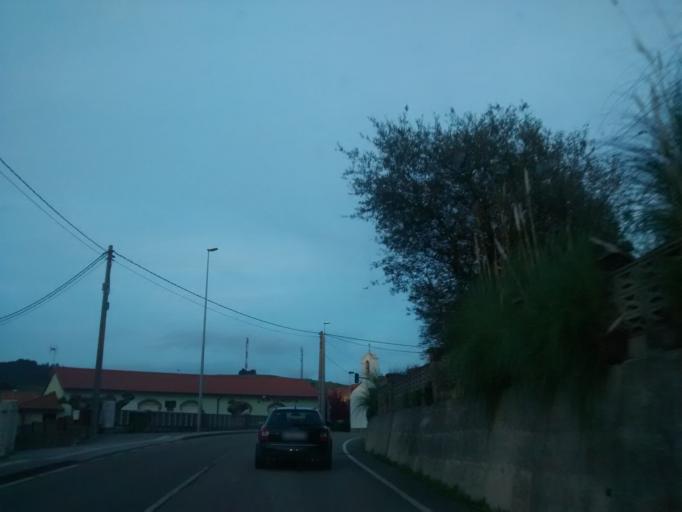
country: ES
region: Cantabria
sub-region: Provincia de Cantabria
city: Santa Cruz de Bezana
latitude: 43.4260
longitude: -3.9410
